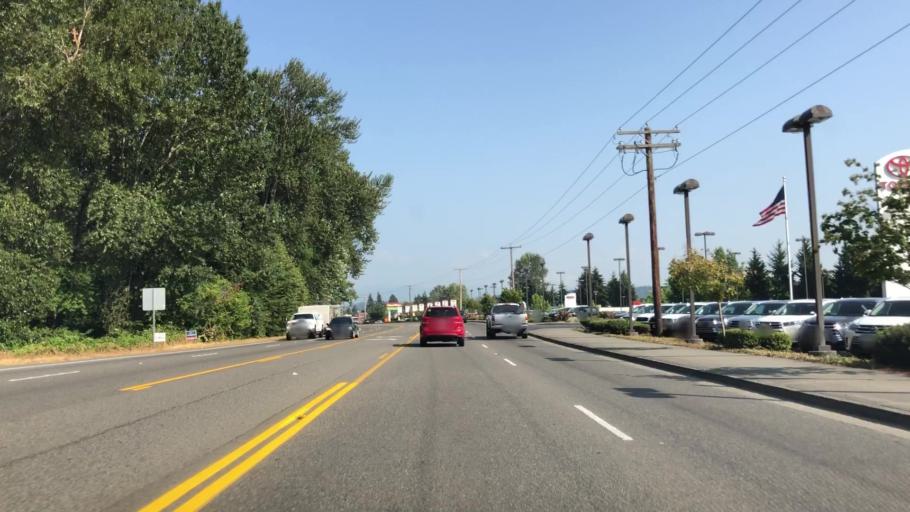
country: US
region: Washington
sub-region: Pierce County
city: Puyallup
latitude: 47.2041
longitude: -122.3130
